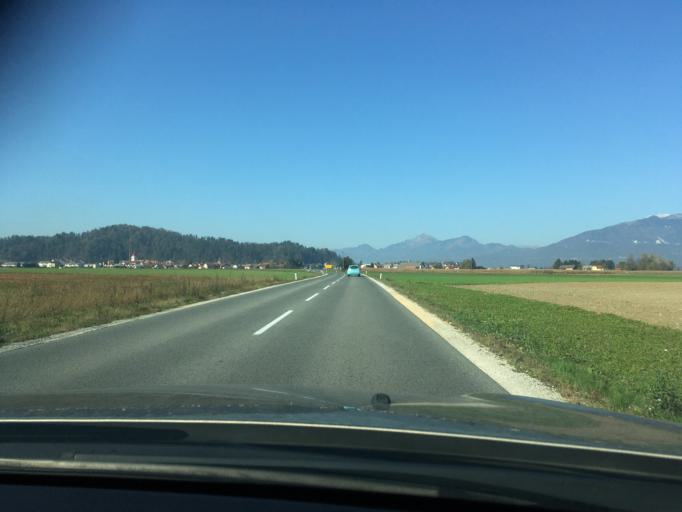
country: SI
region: Menges
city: Menges
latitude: 46.1571
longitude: 14.5845
